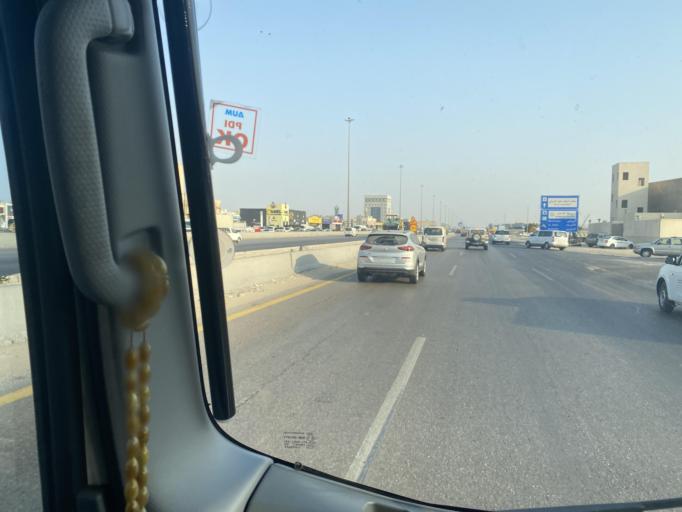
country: SA
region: Eastern Province
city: Sayhat
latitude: 26.4030
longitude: 50.0157
